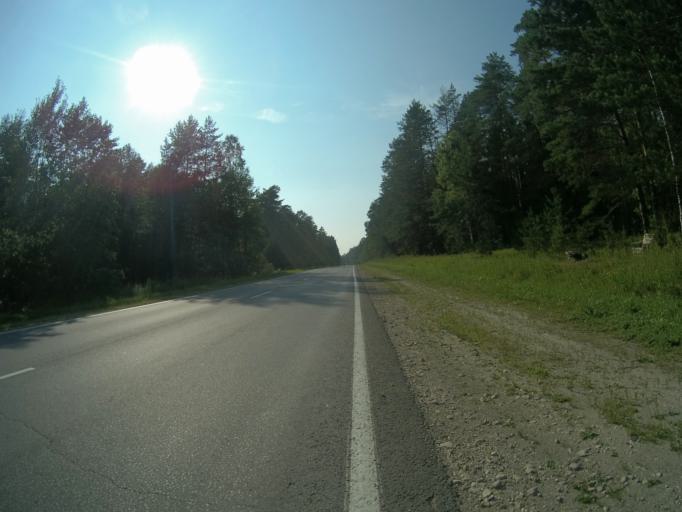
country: RU
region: Vladimir
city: Muromtsevo
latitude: 55.9551
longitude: 40.9988
